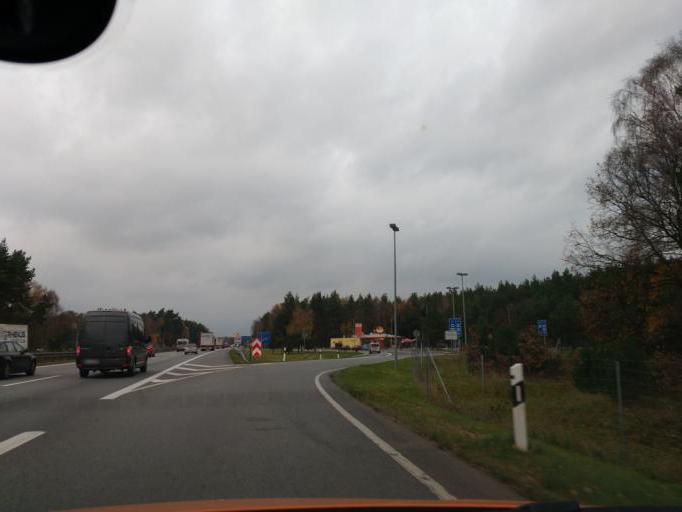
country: DE
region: Brandenburg
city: Wittstock
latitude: 53.1139
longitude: 12.4695
